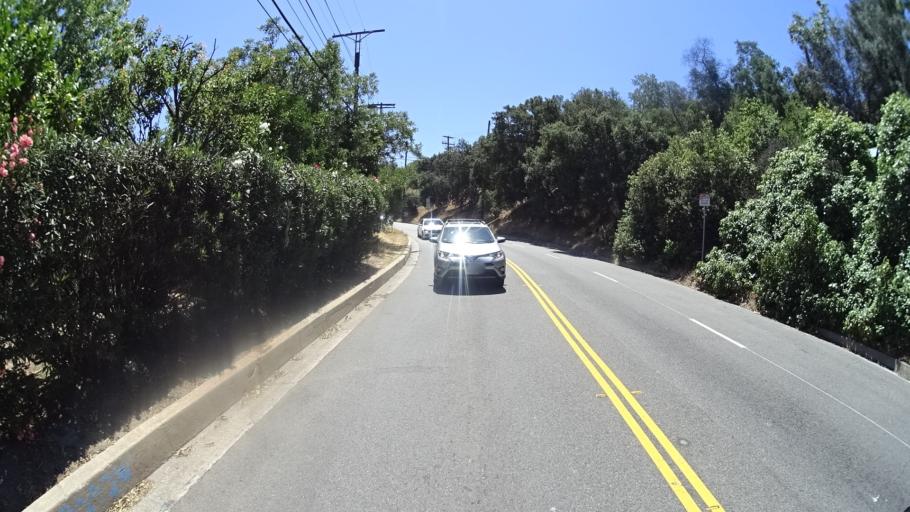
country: US
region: California
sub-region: Los Angeles County
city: Sherman Oaks
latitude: 34.1308
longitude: -118.4440
